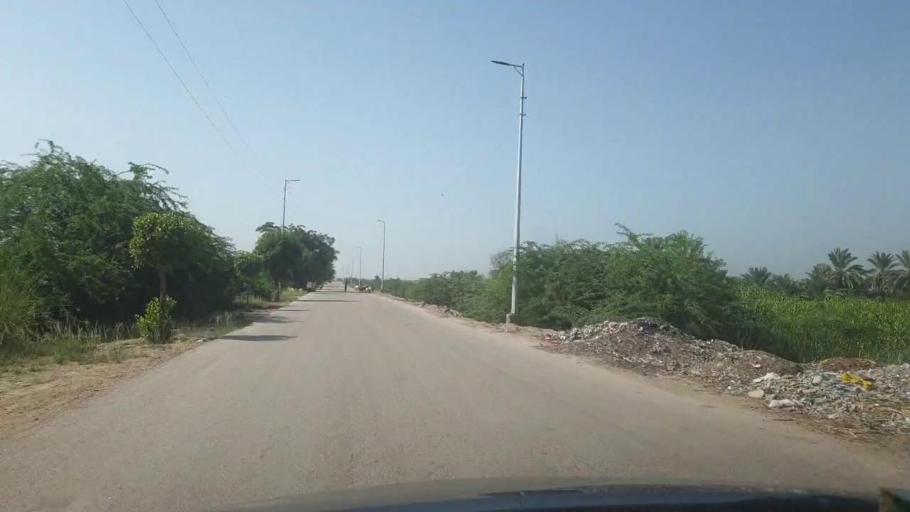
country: PK
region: Sindh
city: Rohri
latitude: 27.5104
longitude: 69.0360
